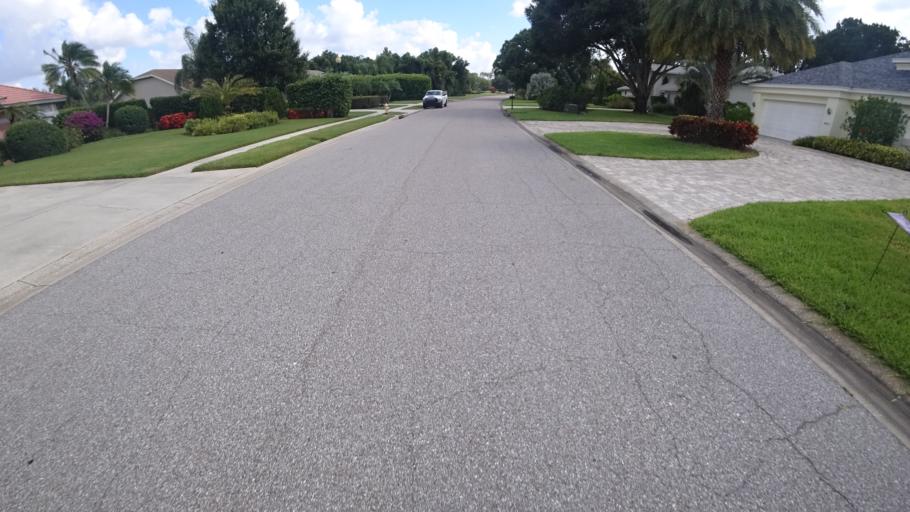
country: US
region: Florida
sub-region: Sarasota County
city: The Meadows
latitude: 27.4303
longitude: -82.4400
